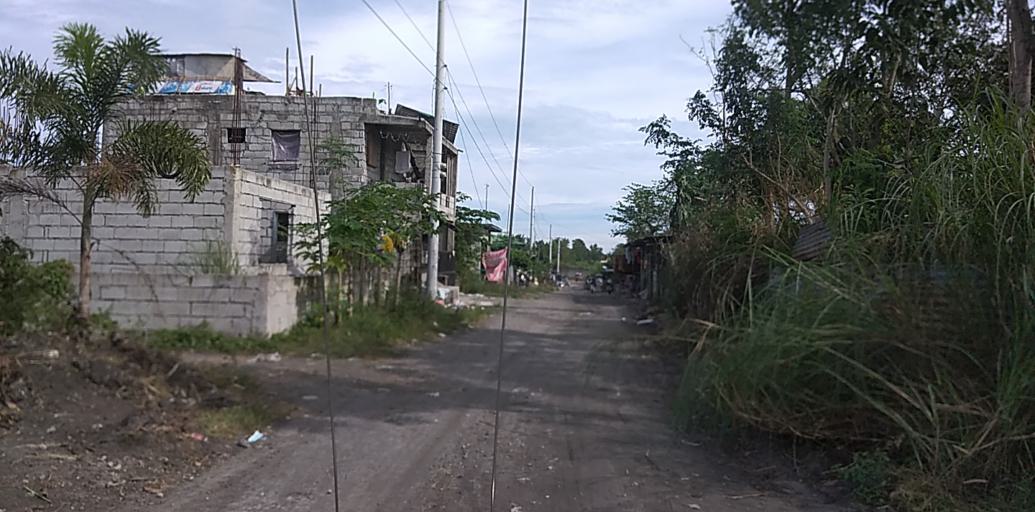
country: PH
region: Central Luzon
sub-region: Province of Pampanga
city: Manibaug Pasig
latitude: 15.1292
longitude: 120.5557
